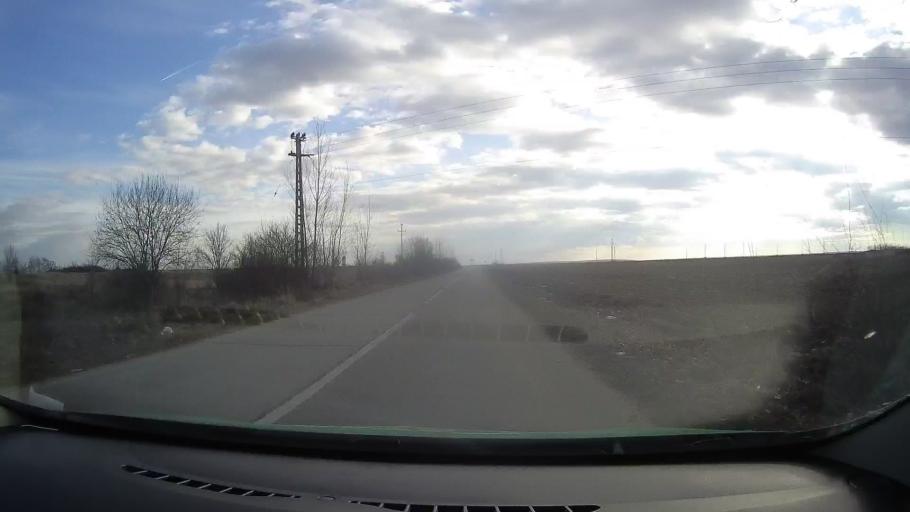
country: RO
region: Dambovita
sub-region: Comuna Ulmi
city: Ulmi
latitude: 44.8874
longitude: 25.4650
